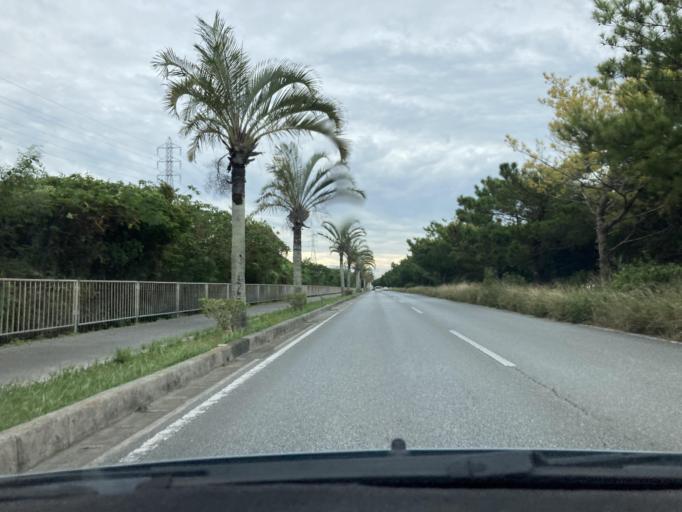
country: JP
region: Okinawa
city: Okinawa
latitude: 26.3909
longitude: 127.7553
